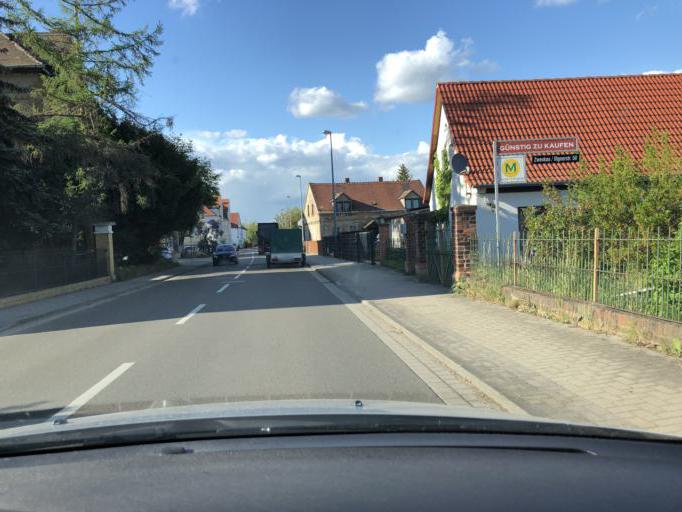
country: DE
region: Saxony
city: Bohlen
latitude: 51.2357
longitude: 12.3850
